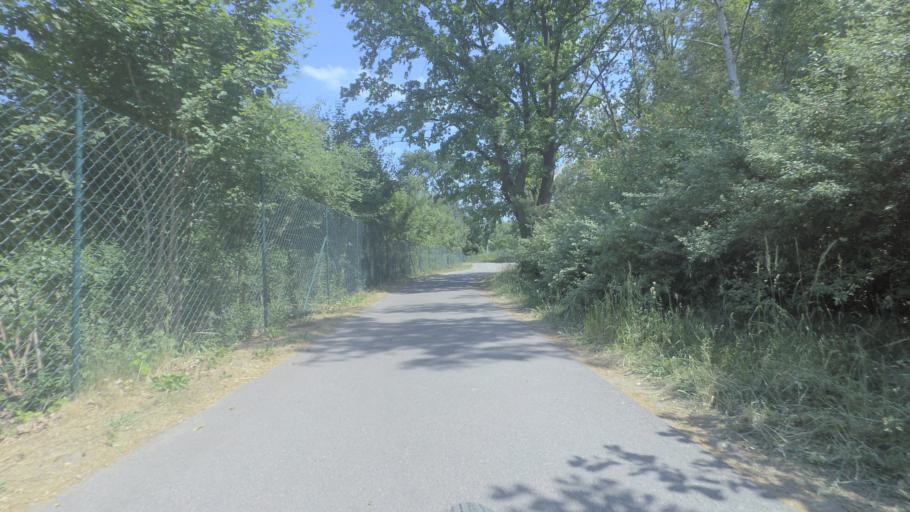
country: DE
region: Saxony-Anhalt
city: Wittenburg
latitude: 51.8434
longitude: 12.6201
